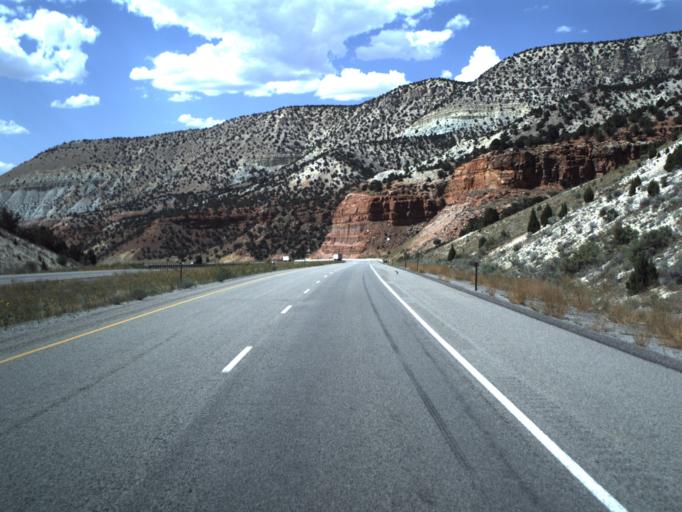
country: US
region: Utah
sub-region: Sevier County
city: Salina
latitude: 38.9277
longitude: -111.7829
